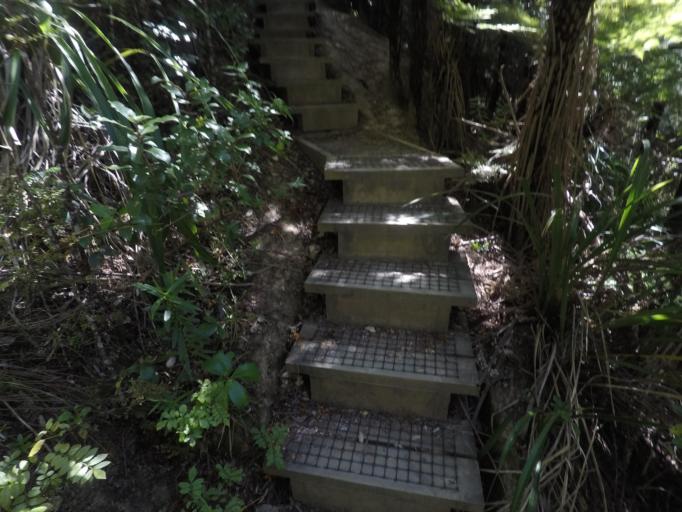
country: NZ
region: Auckland
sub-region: Auckland
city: North Shore
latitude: -36.8223
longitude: 174.7071
